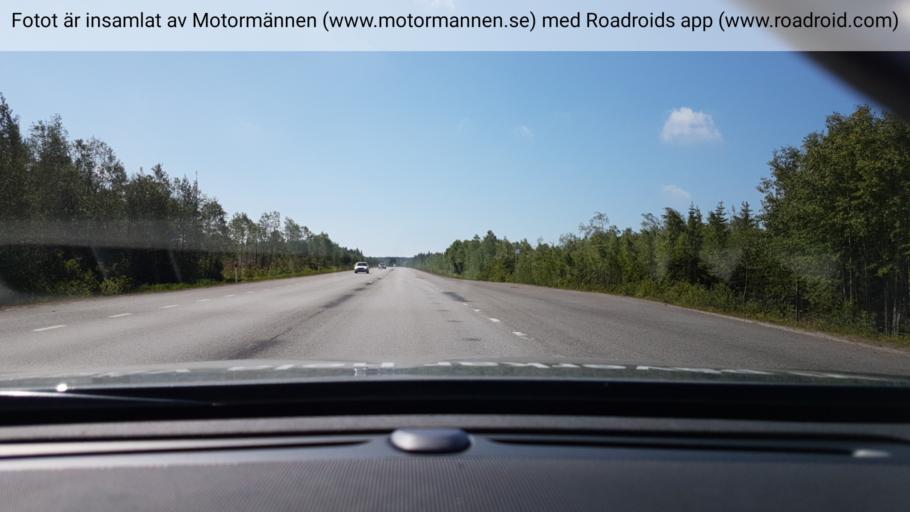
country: SE
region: Vaesterbotten
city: Obbola
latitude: 63.7242
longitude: 20.3162
